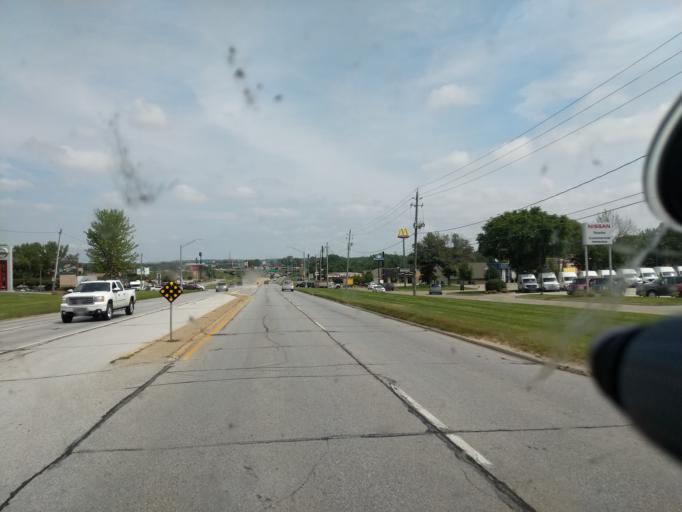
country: US
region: Iowa
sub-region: Polk County
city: Urbandale
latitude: 41.6474
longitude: -93.6979
